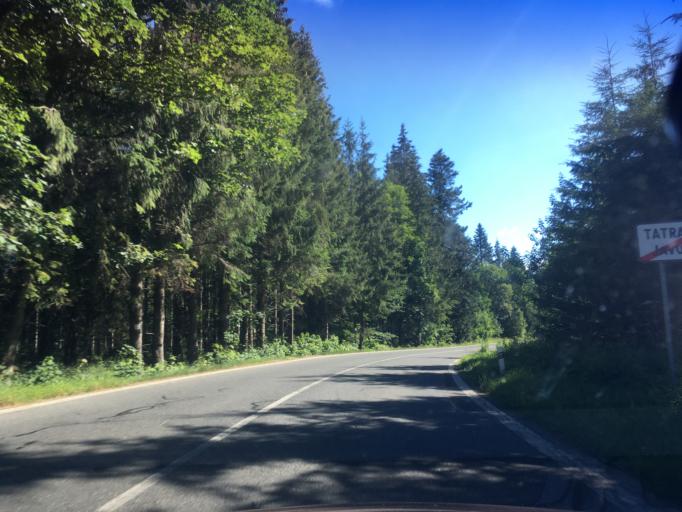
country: PL
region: Lesser Poland Voivodeship
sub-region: Powiat tatrzanski
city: Bukowina Tatrzanska
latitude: 49.2705
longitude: 20.1486
